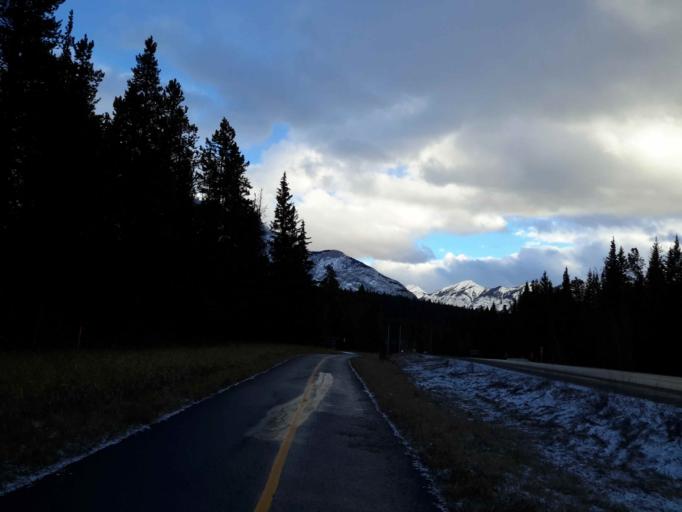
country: CA
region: Alberta
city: Banff
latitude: 51.2037
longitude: -115.5372
